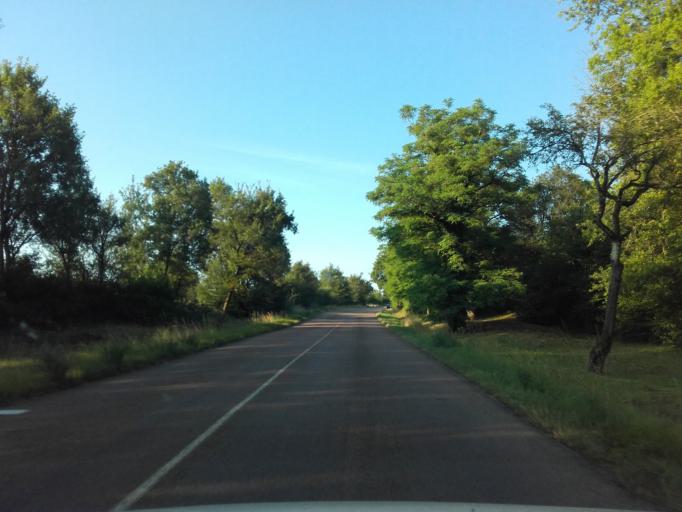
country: FR
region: Bourgogne
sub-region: Departement de Saone-et-Loire
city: Dracy-le-Fort
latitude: 46.7994
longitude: 4.7520
